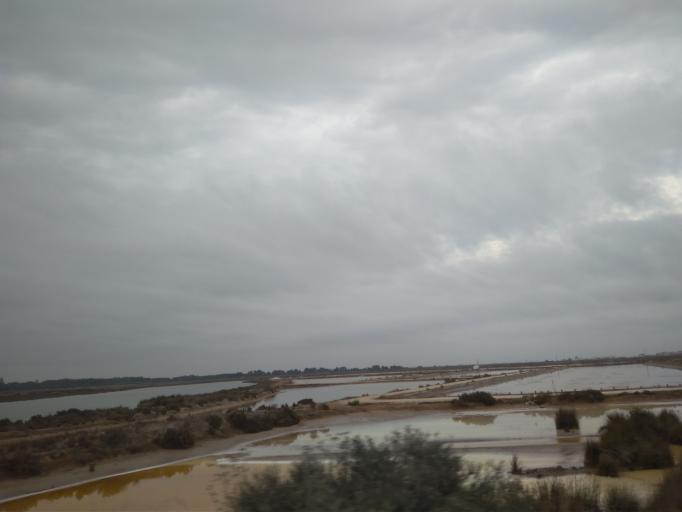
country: PT
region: Faro
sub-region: Faro
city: Faro
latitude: 37.0314
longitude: -7.9956
